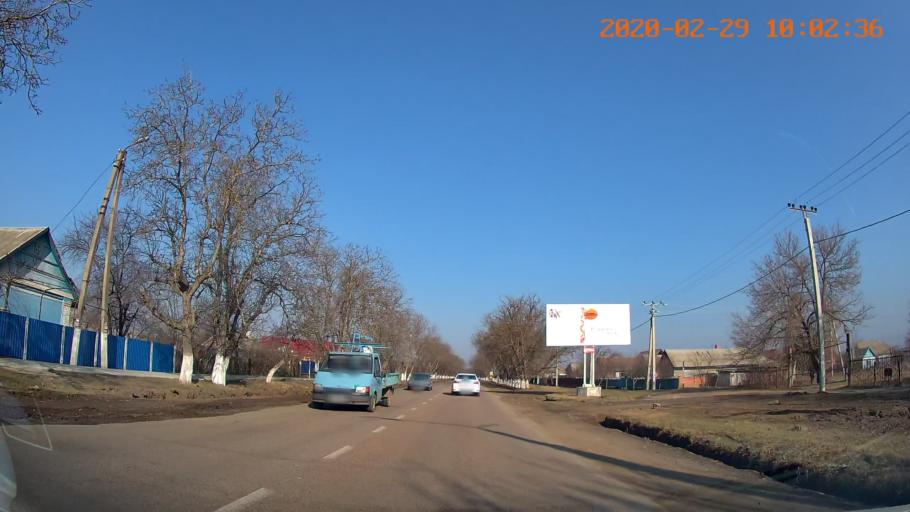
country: MD
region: Telenesti
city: Slobozia
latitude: 46.7842
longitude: 29.6831
